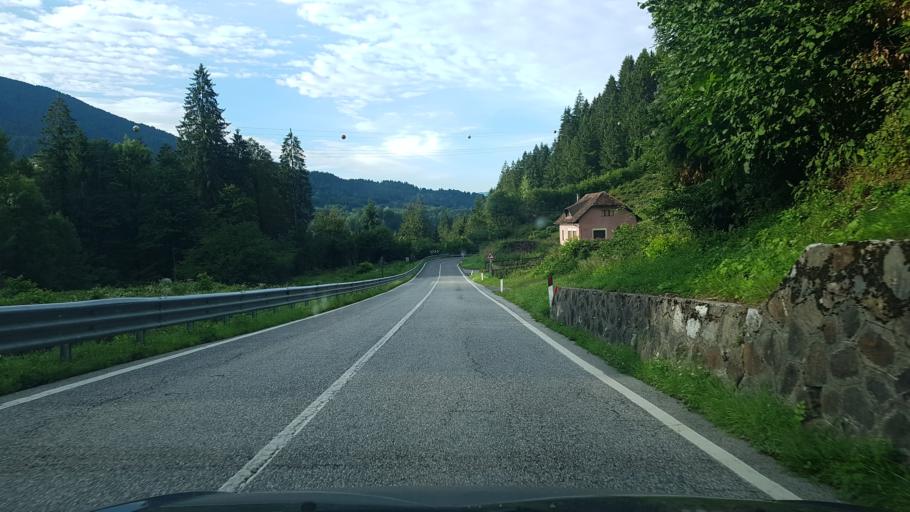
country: IT
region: Friuli Venezia Giulia
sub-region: Provincia di Udine
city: Comeglians
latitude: 46.5286
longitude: 12.8698
